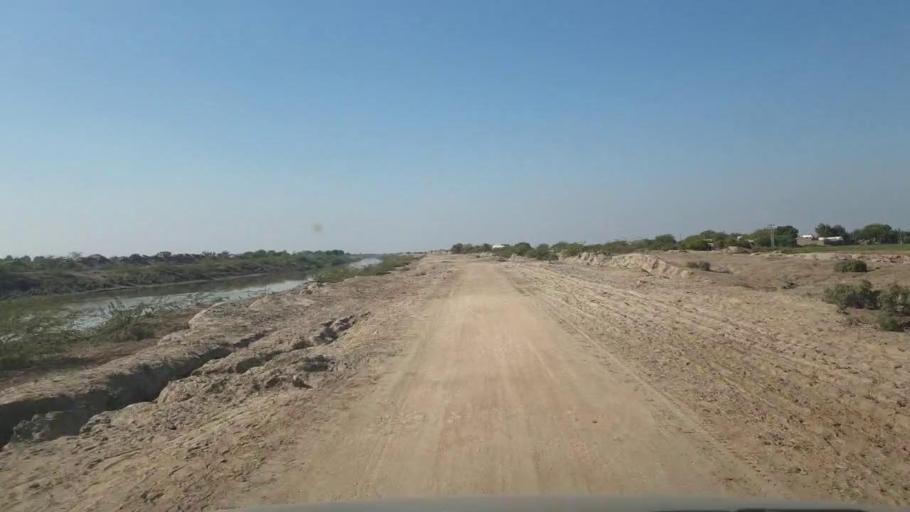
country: PK
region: Sindh
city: Pithoro
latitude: 25.4035
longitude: 69.2584
